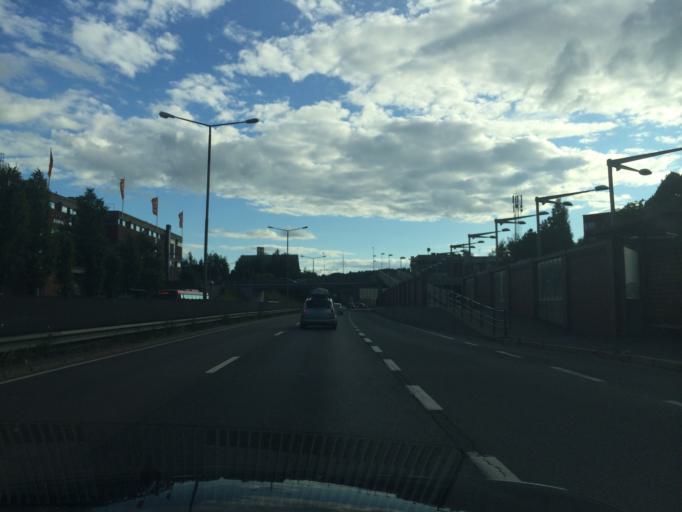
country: NO
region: Oslo
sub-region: Oslo
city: Oslo
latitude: 59.8984
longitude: 10.8141
